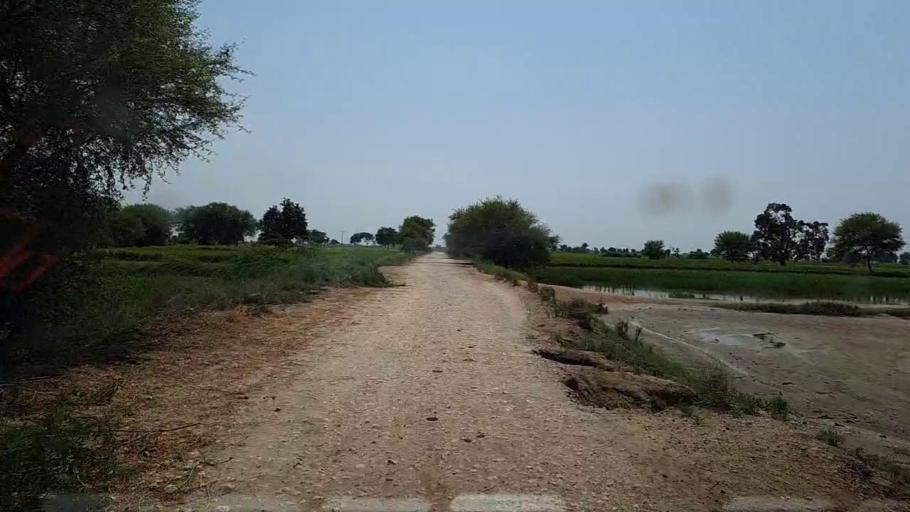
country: PK
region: Sindh
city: Kario
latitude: 24.6420
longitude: 68.4860
